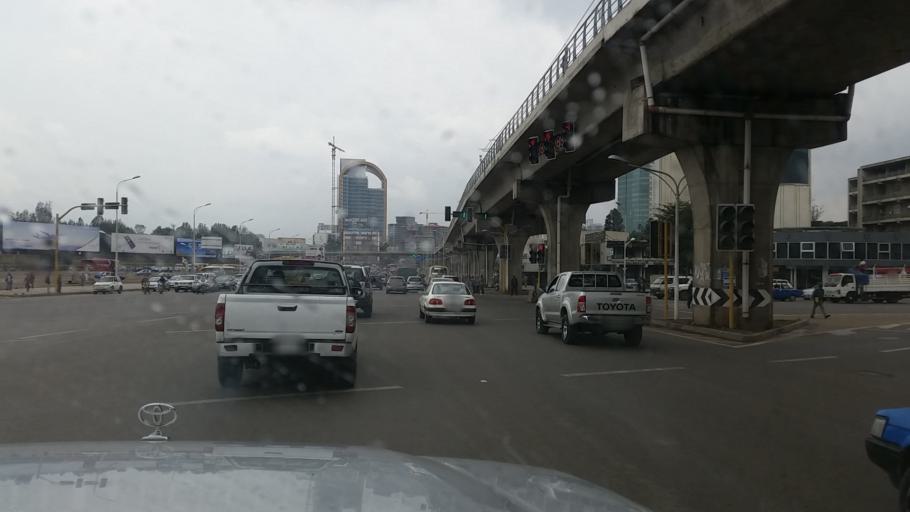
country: ET
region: Adis Abeba
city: Addis Ababa
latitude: 9.0109
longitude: 38.7632
